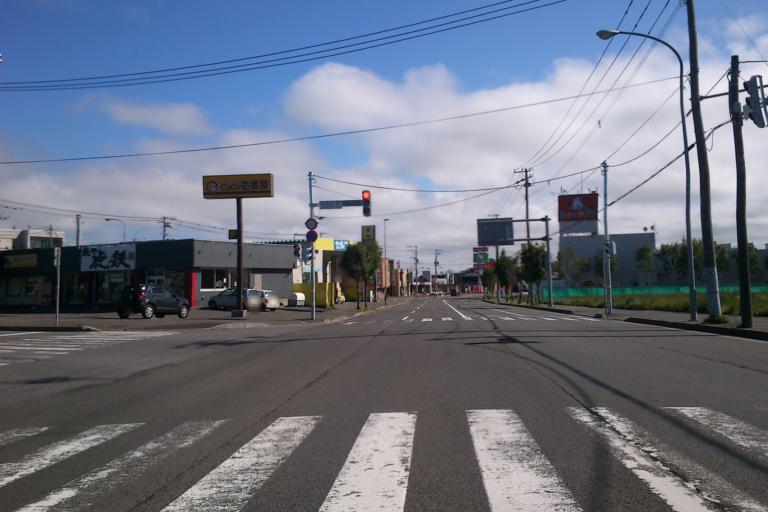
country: JP
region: Hokkaido
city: Sapporo
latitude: 43.1206
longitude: 141.2483
